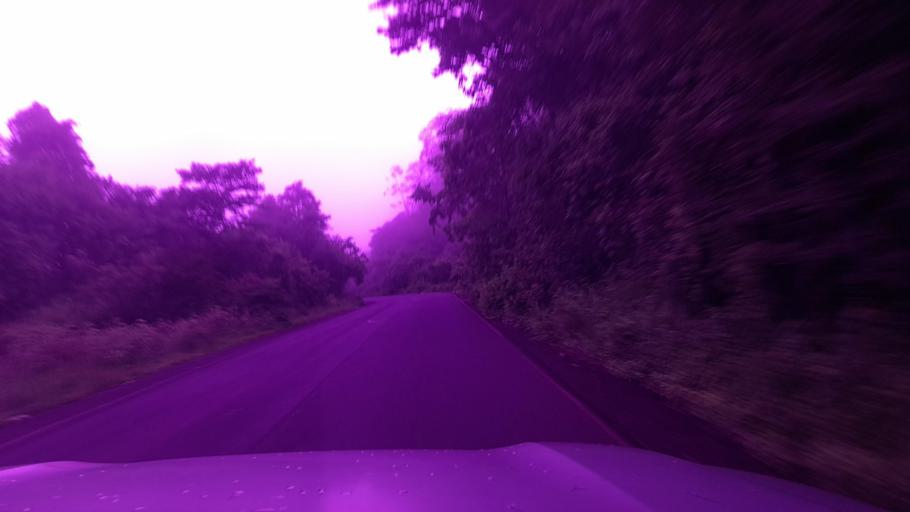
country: ET
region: Oromiya
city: Waliso
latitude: 8.1697
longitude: 37.5493
